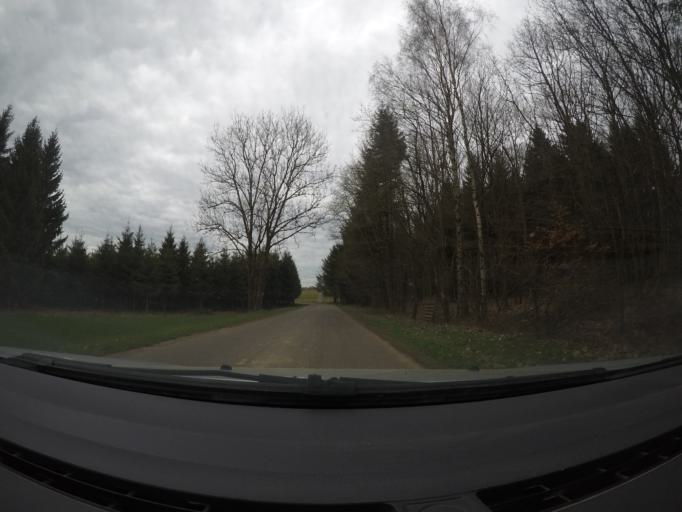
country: BE
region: Wallonia
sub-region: Province du Luxembourg
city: Leglise
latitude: 49.7782
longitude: 5.5861
